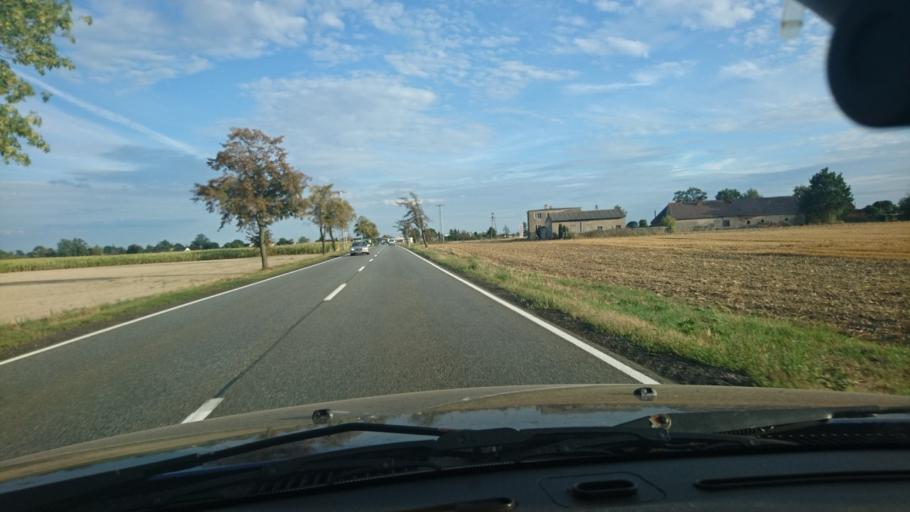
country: PL
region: Opole Voivodeship
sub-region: Powiat kluczborski
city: Kluczbork
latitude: 51.0133
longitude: 18.2019
